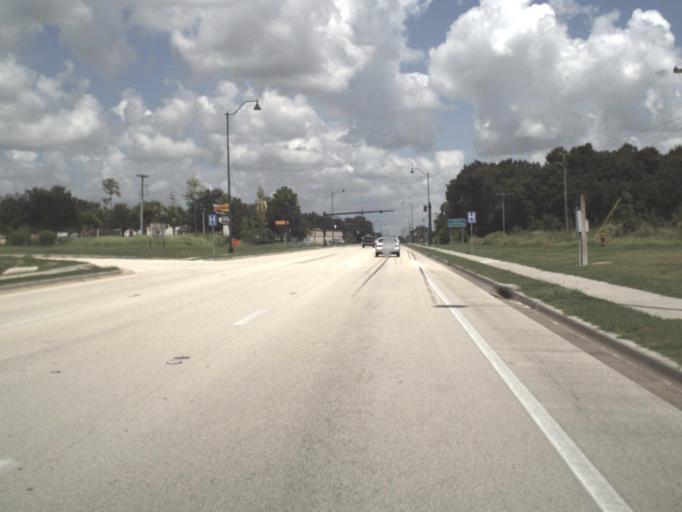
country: US
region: Florida
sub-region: Hardee County
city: Wauchula
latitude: 27.5349
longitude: -81.8075
